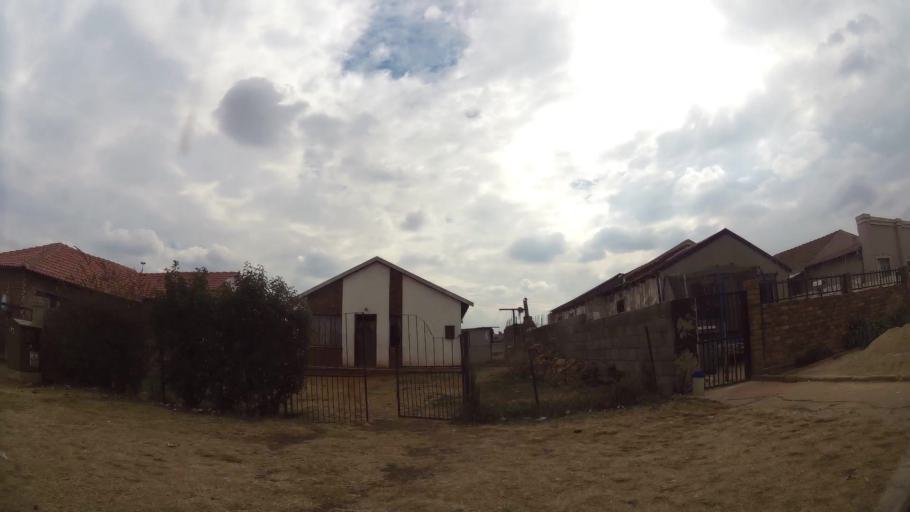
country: ZA
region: Gauteng
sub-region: Ekurhuleni Metropolitan Municipality
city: Germiston
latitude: -26.3859
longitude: 28.1296
